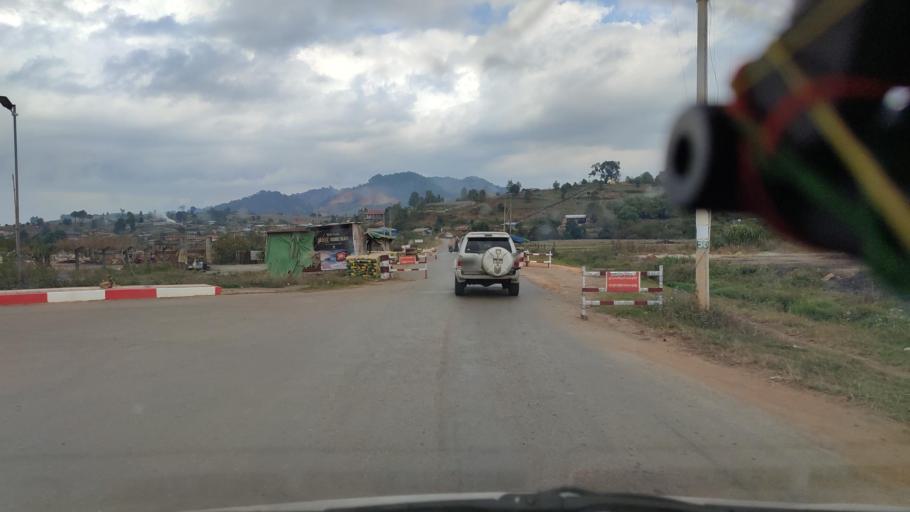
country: MM
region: Shan
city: Taunggyi
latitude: 21.0129
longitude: 97.5398
